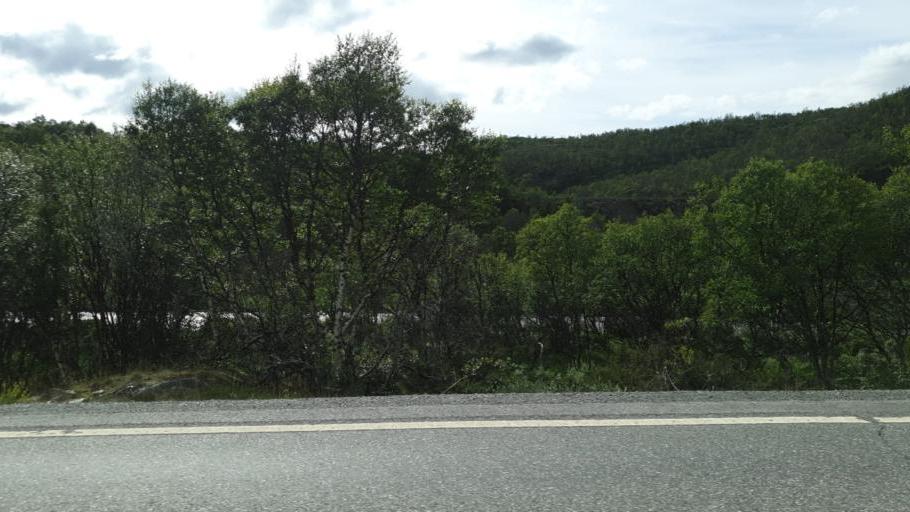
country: NO
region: Sor-Trondelag
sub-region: Oppdal
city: Oppdal
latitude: 62.2918
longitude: 9.5950
